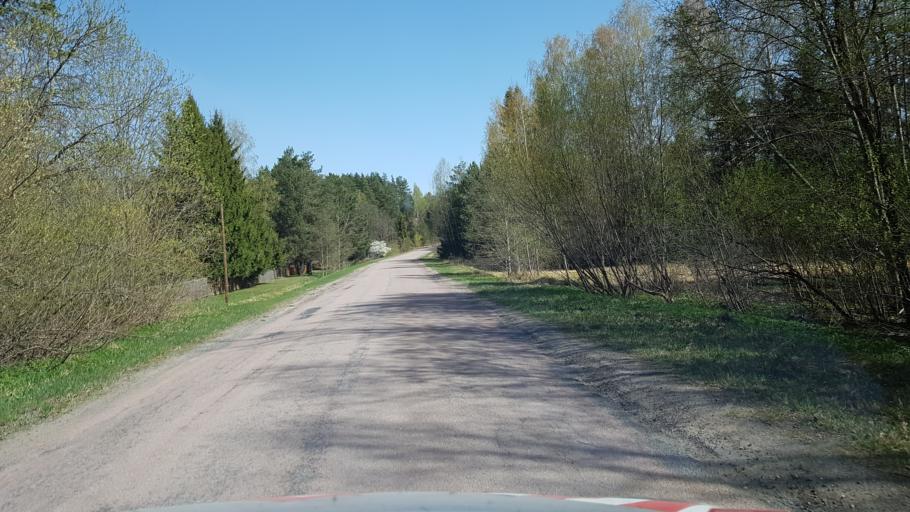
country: EE
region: Tartu
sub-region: Elva linn
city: Elva
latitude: 58.2407
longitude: 26.4188
